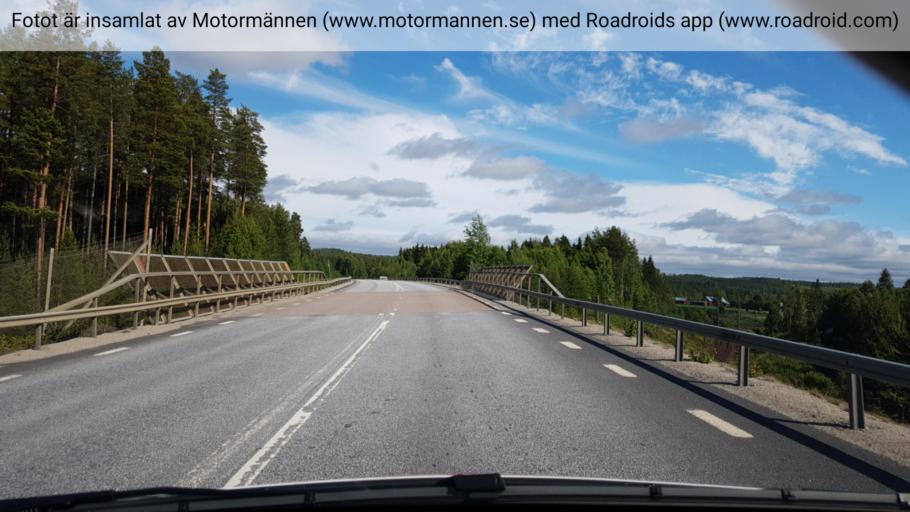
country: SE
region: Vaesterbotten
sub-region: Vannas Kommun
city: Vaennaes
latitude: 64.0082
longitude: 19.7038
